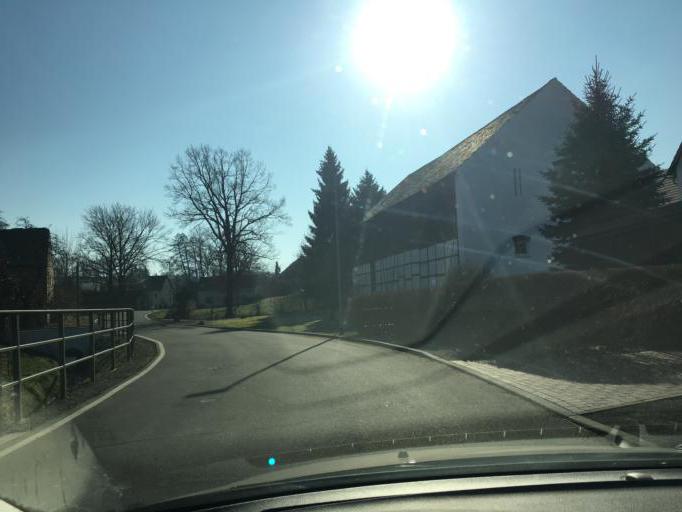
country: DE
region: Saxony
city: Geithain
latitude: 51.0438
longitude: 12.7097
